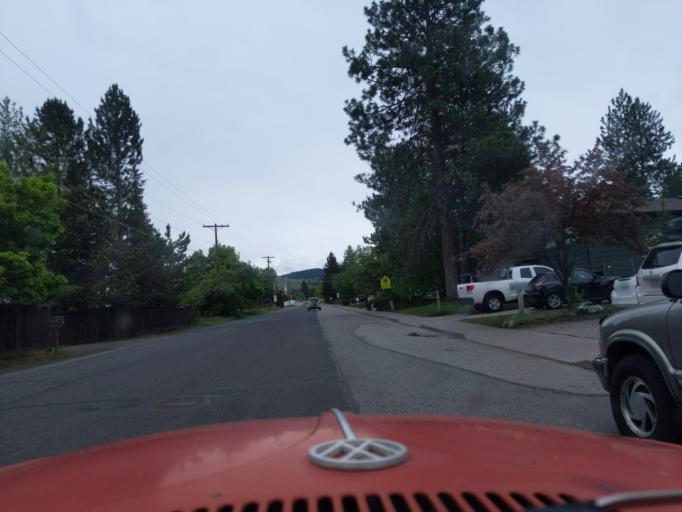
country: US
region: Washington
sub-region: Spokane County
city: Spokane
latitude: 47.5968
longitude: -117.3772
